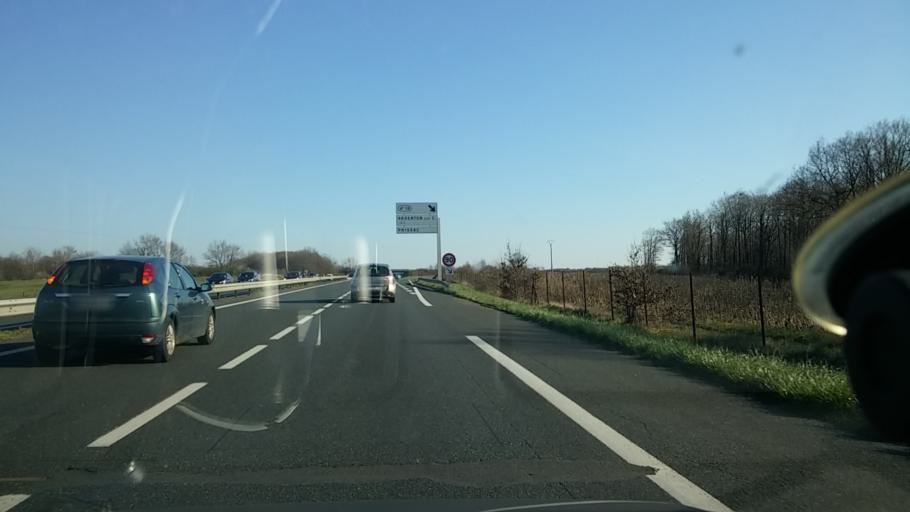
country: FR
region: Centre
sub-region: Departement de l'Indre
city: Argenton-sur-Creuse
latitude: 46.5742
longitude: 1.4984
